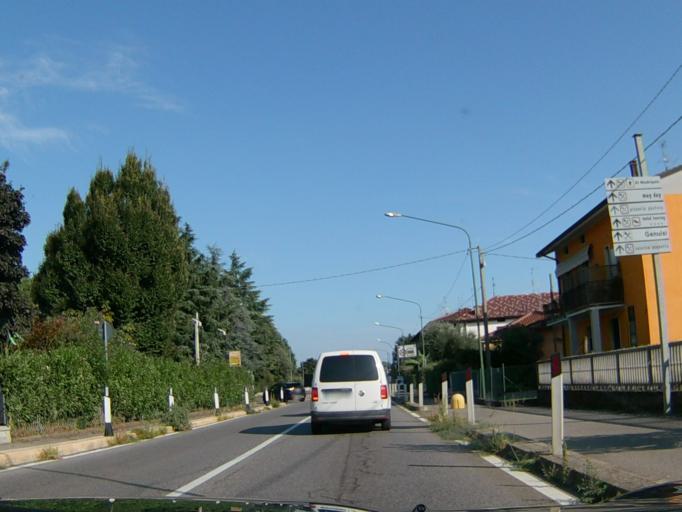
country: IT
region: Lombardy
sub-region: Provincia di Brescia
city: Coccaglio
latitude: 45.5682
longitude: 9.9658
